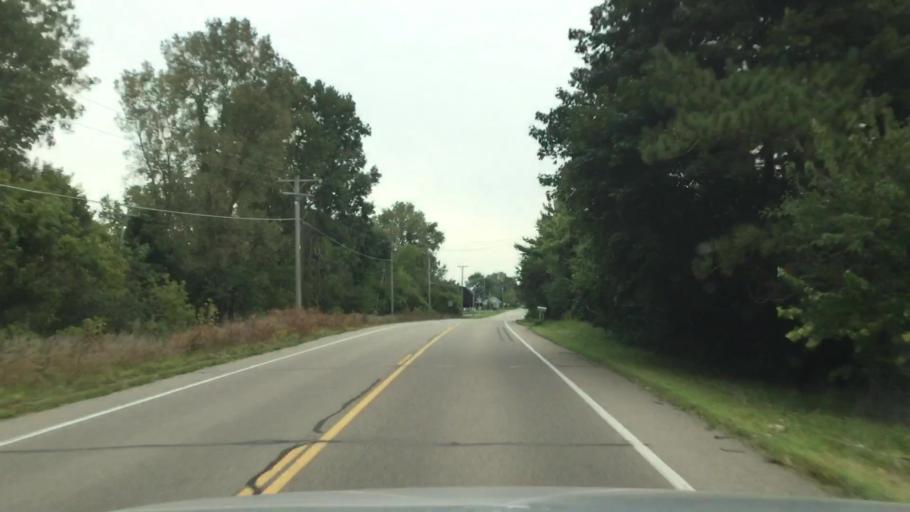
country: US
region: Michigan
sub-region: Washtenaw County
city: Milan
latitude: 42.1225
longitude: -83.7000
